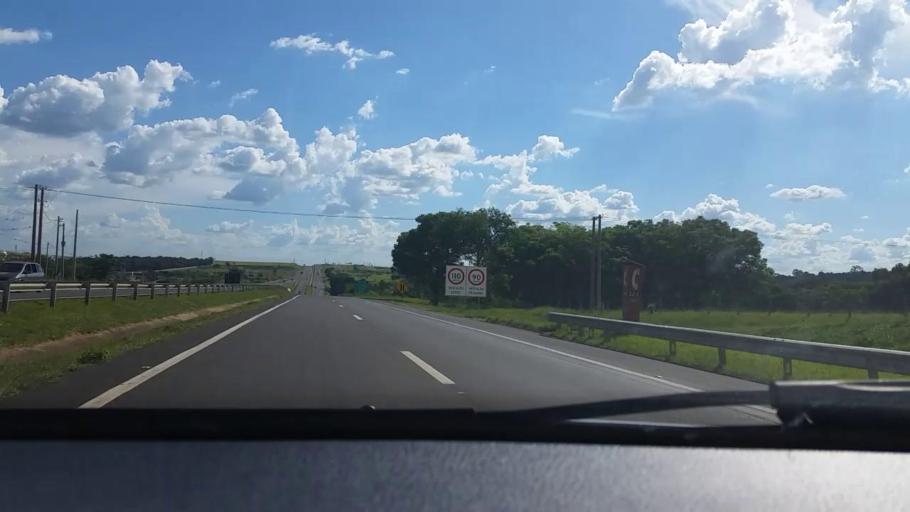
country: BR
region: Sao Paulo
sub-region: Bauru
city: Bauru
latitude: -22.3810
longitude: -49.0654
